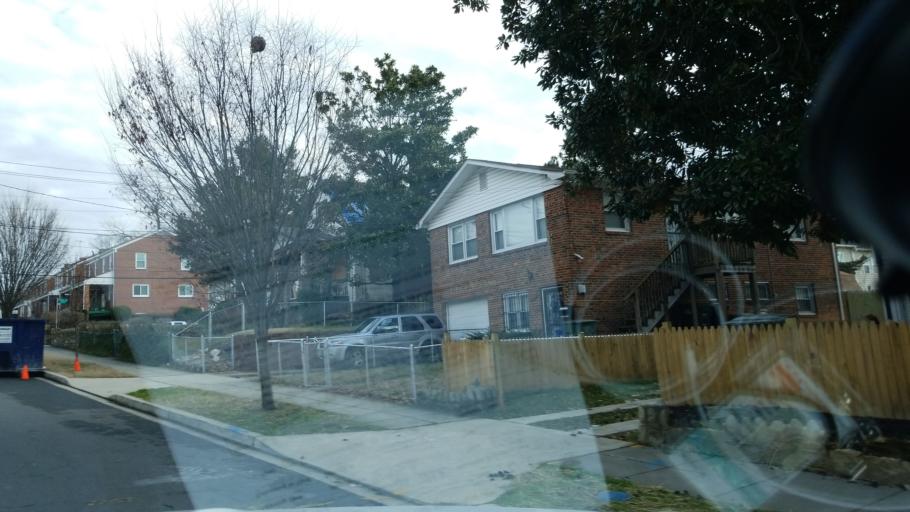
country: US
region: Maryland
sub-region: Prince George's County
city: Glassmanor
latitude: 38.8411
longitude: -76.9918
